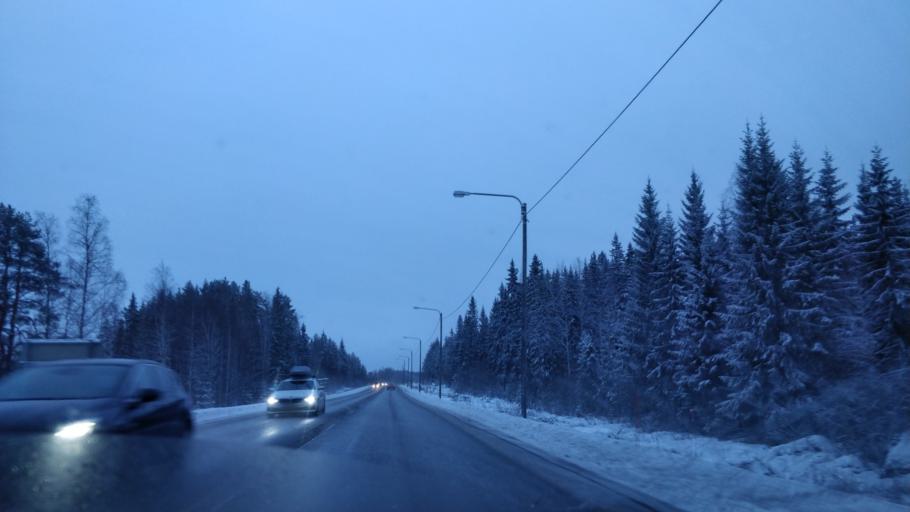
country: FI
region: Central Finland
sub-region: AEaenekoski
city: AEaenekoski
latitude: 62.8163
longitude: 25.8034
